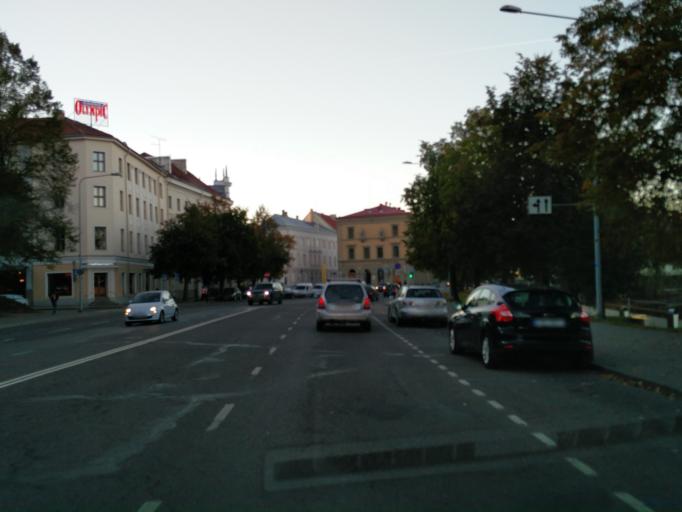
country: EE
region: Tartu
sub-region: Tartu linn
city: Tartu
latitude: 58.3796
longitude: 26.7262
